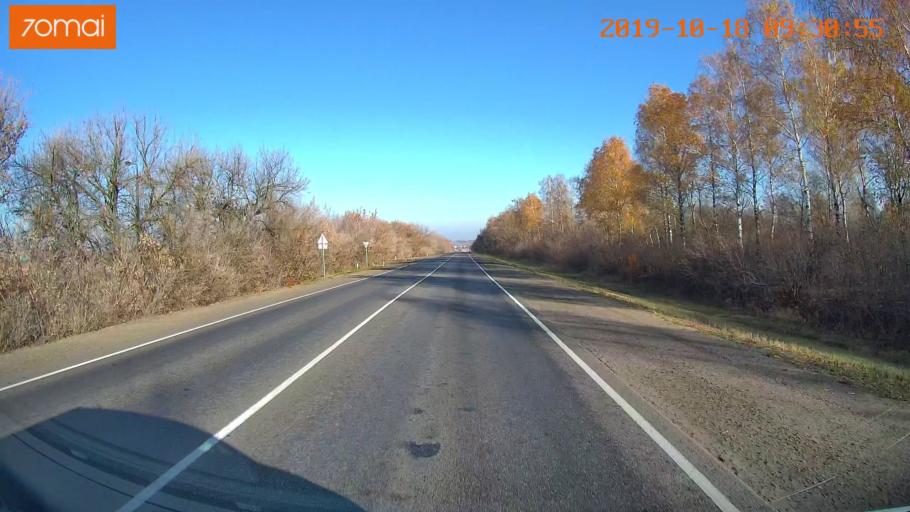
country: RU
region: Tula
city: Yefremov
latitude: 53.1441
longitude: 38.1589
